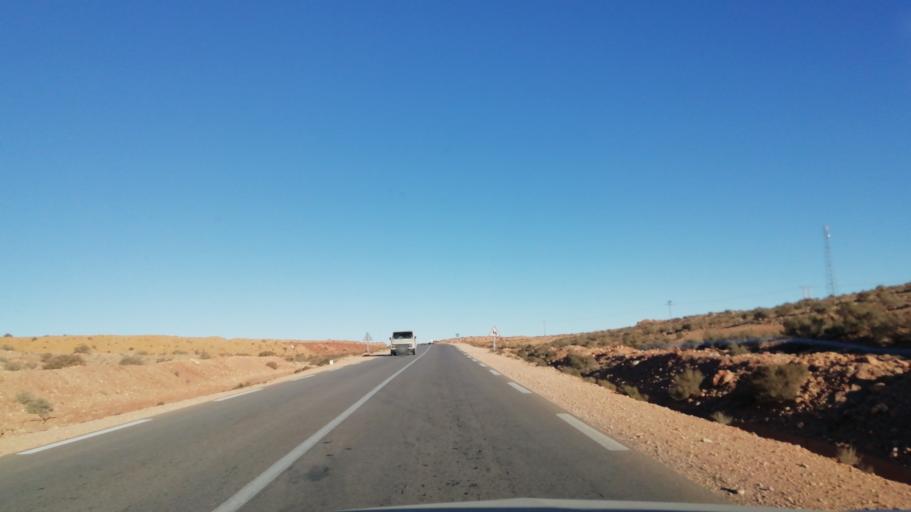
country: DZ
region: El Bayadh
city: El Abiodh Sidi Cheikh
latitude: 33.1724
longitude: 0.4412
